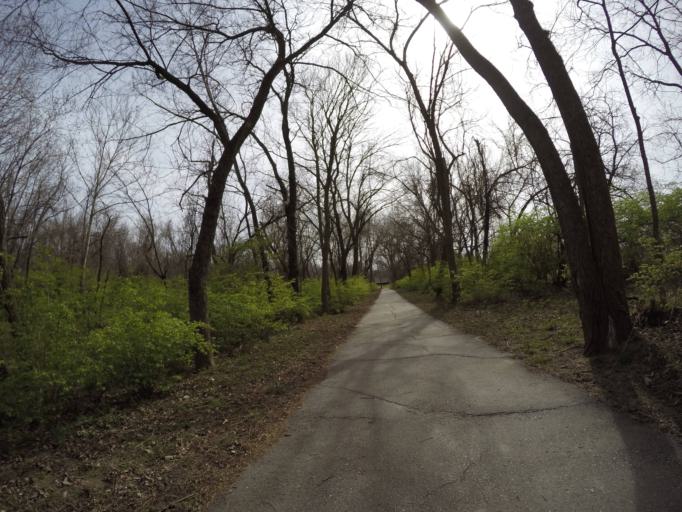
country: US
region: Kansas
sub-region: Johnson County
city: Leawood
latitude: 38.9144
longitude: -94.6326
